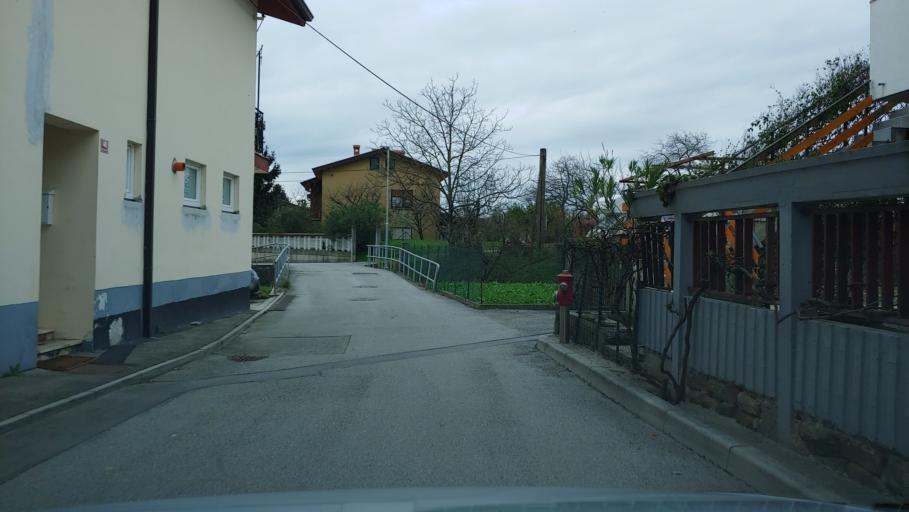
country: SI
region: Sempeter-Vrtojba
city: Vrtojba
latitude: 45.9148
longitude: 13.6400
